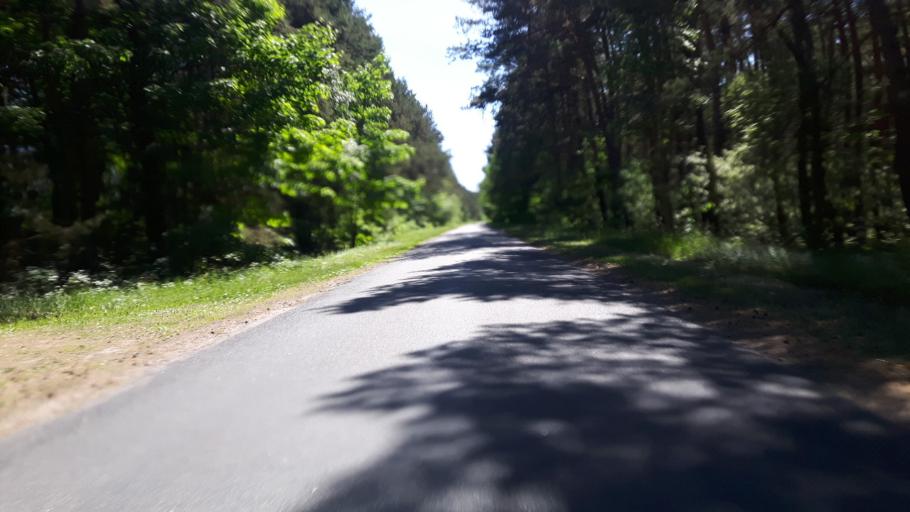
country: LV
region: Salacgrivas
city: Ainazi
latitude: 57.8960
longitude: 24.3731
